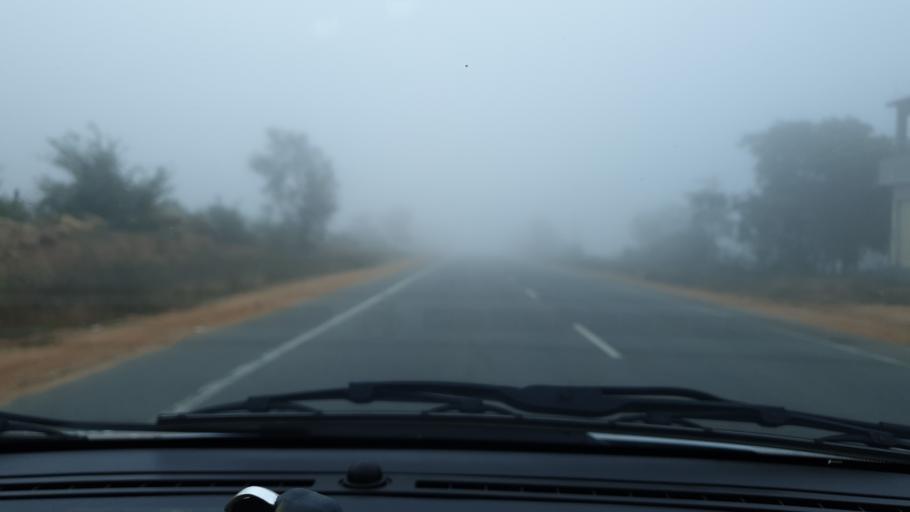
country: IN
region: Telangana
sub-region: Mahbubnagar
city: Nagar Karnul
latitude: 16.6793
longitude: 78.5274
